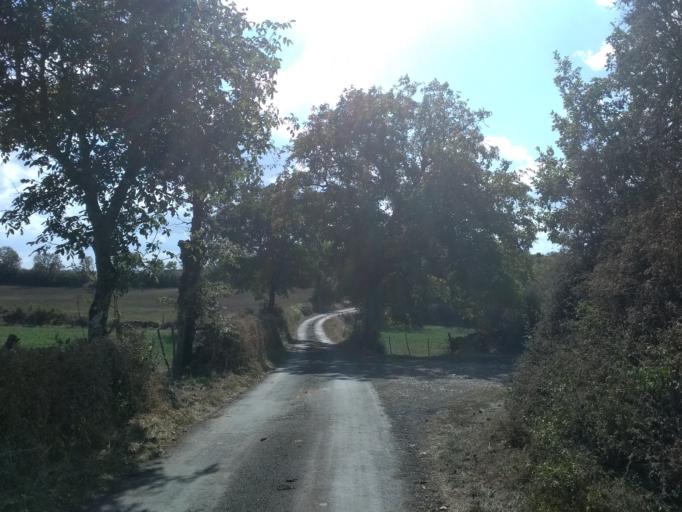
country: FR
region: Midi-Pyrenees
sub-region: Departement de l'Aveyron
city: Bozouls
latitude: 44.4627
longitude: 2.6872
